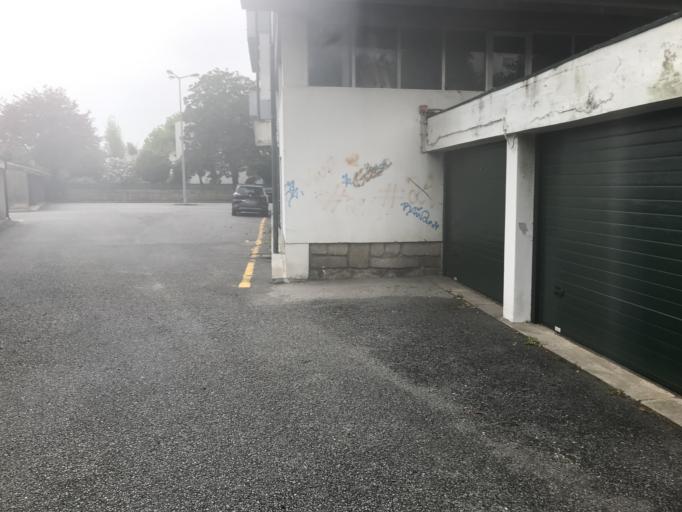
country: PT
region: Porto
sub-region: Matosinhos
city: Senhora da Hora
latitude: 41.1778
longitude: -8.6607
